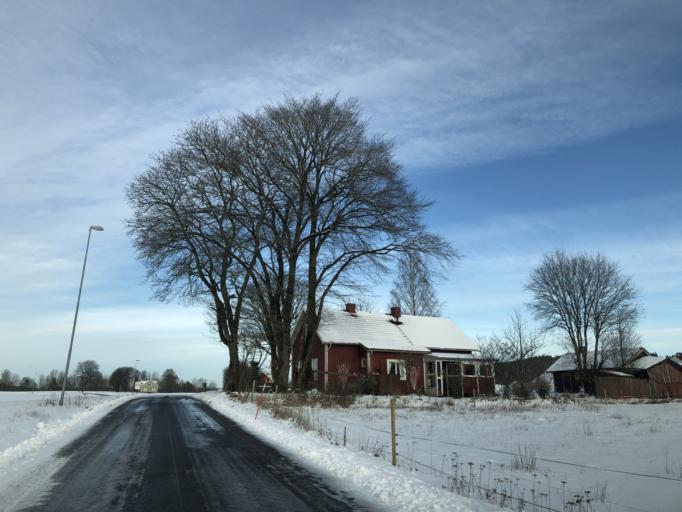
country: SE
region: Vaestra Goetaland
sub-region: Ulricehamns Kommun
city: Ulricehamn
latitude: 57.7835
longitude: 13.5257
